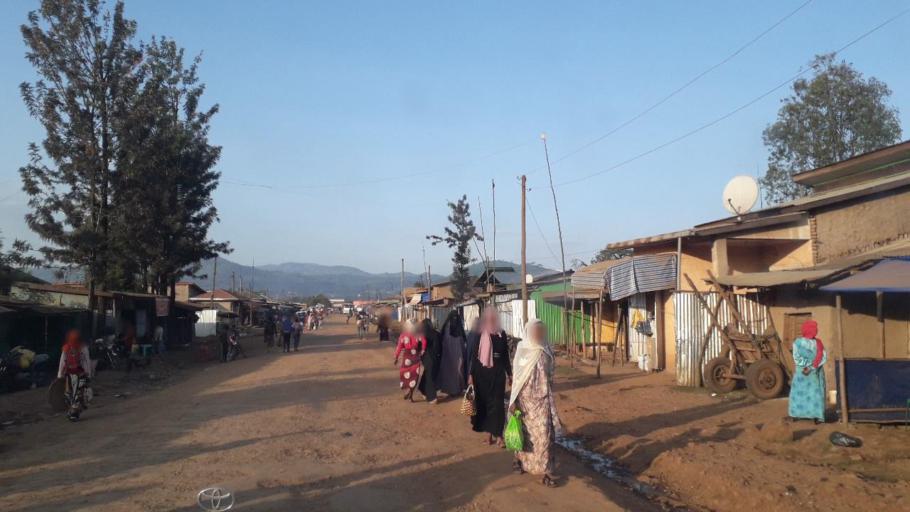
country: ET
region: Oromiya
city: Jima
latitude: 7.6423
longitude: 36.8426
